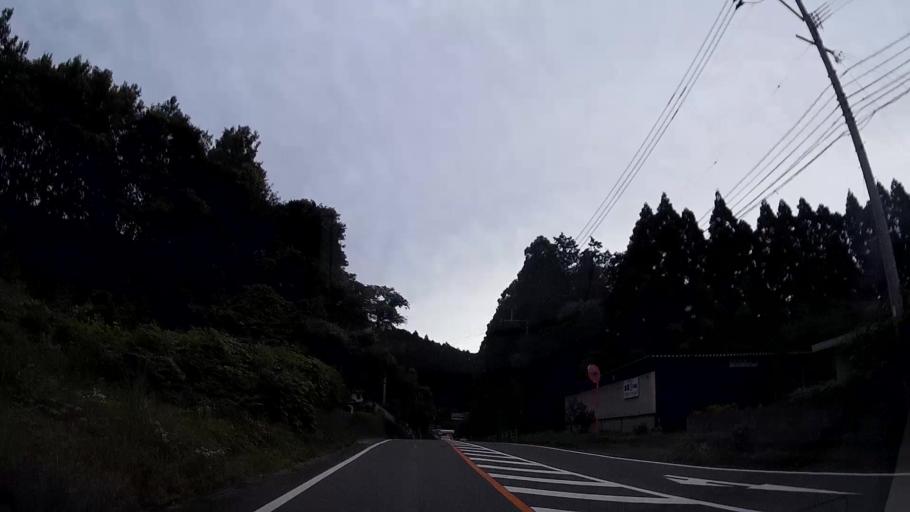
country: JP
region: Kumamoto
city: Kikuchi
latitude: 33.0160
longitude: 130.8650
